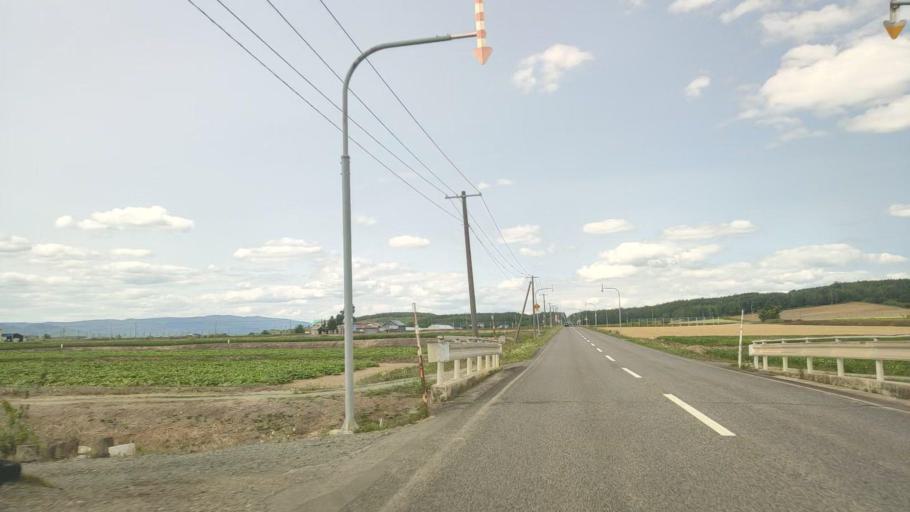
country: JP
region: Hokkaido
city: Nayoro
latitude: 44.2326
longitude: 142.4157
